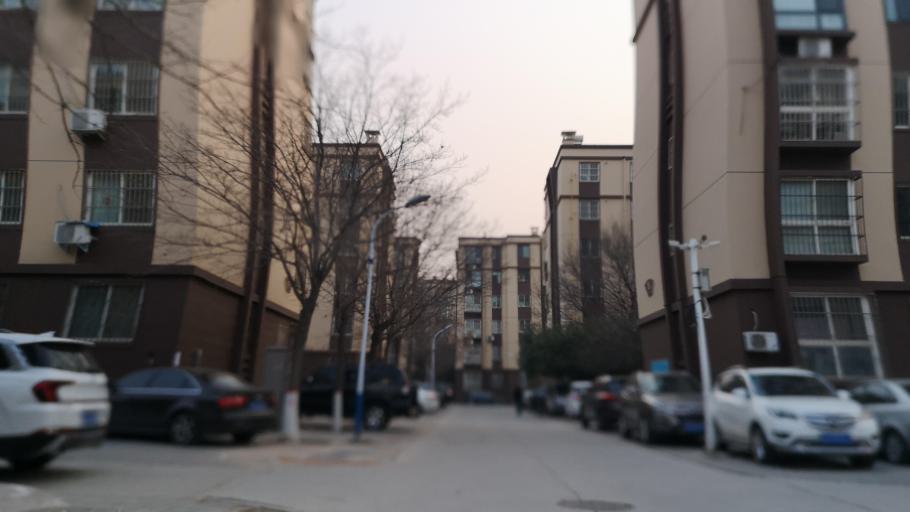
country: CN
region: Henan Sheng
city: Zhongyuanlu
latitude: 35.7863
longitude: 115.0805
